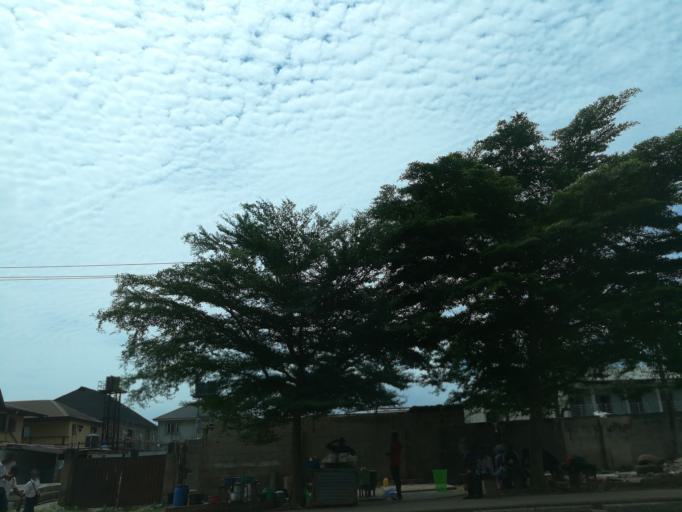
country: NG
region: Lagos
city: Ebute Ikorodu
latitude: 6.5606
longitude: 3.4759
